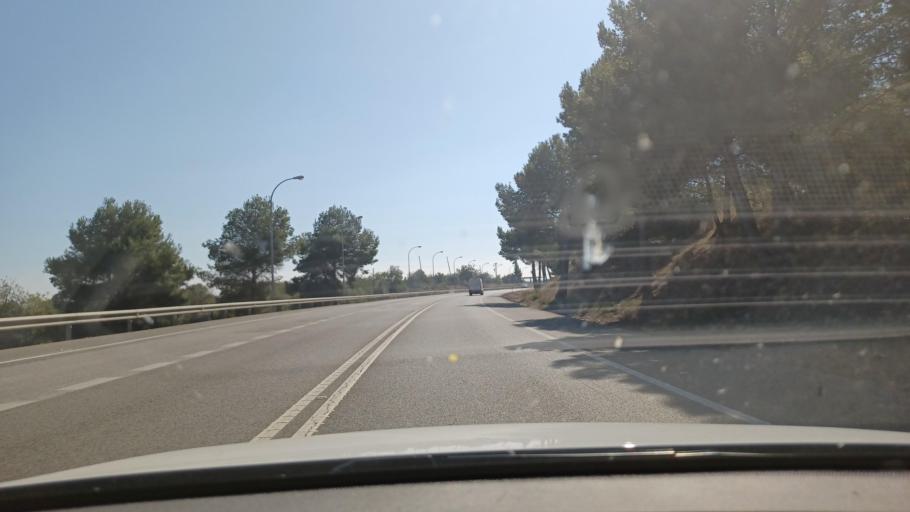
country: ES
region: Catalonia
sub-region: Provincia de Tarragona
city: L'Ampolla
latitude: 40.8412
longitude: 0.7110
